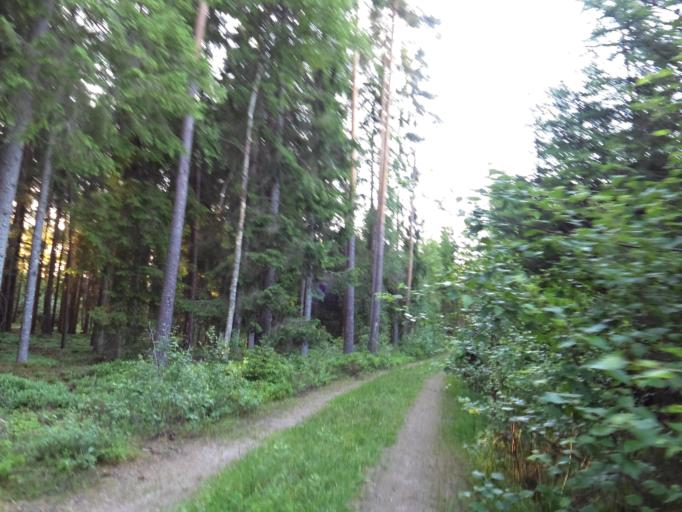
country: SE
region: Blekinge
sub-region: Olofstroms Kommun
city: Olofstroem
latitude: 56.4144
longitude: 14.5555
